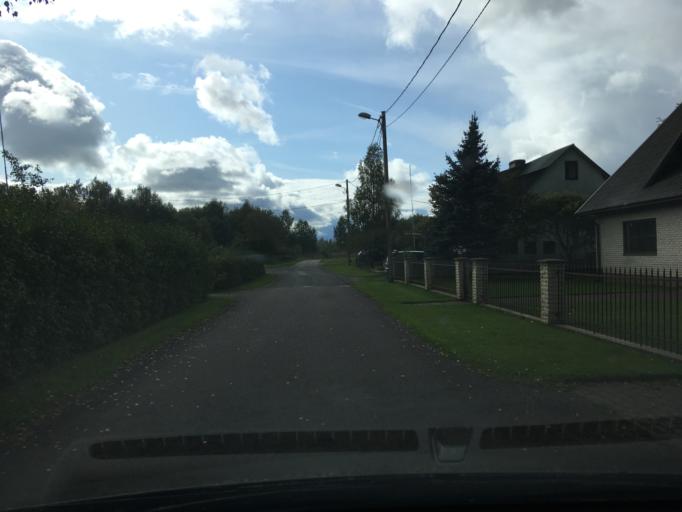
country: EE
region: Raplamaa
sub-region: Rapla vald
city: Rapla
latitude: 58.9902
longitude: 24.8314
